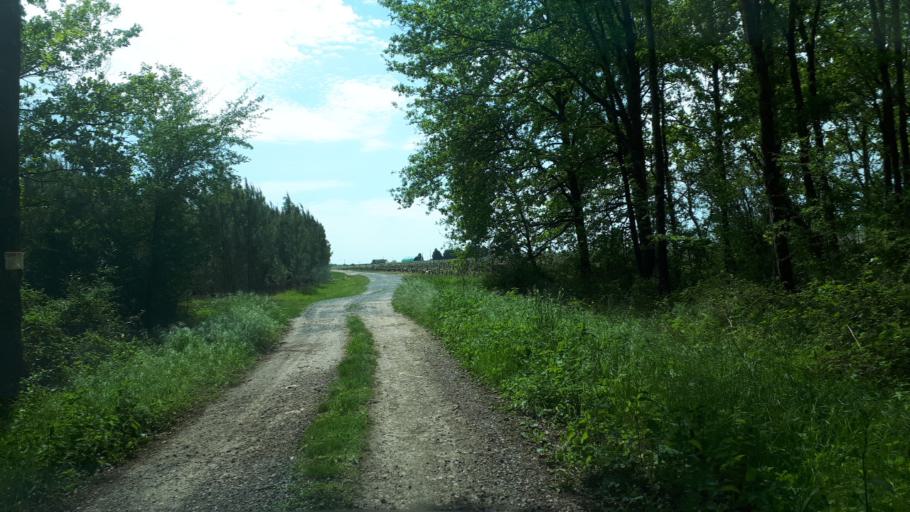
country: FR
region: Centre
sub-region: Departement du Loir-et-Cher
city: Saint-Romain-sur-Cher
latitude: 47.3593
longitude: 1.4295
